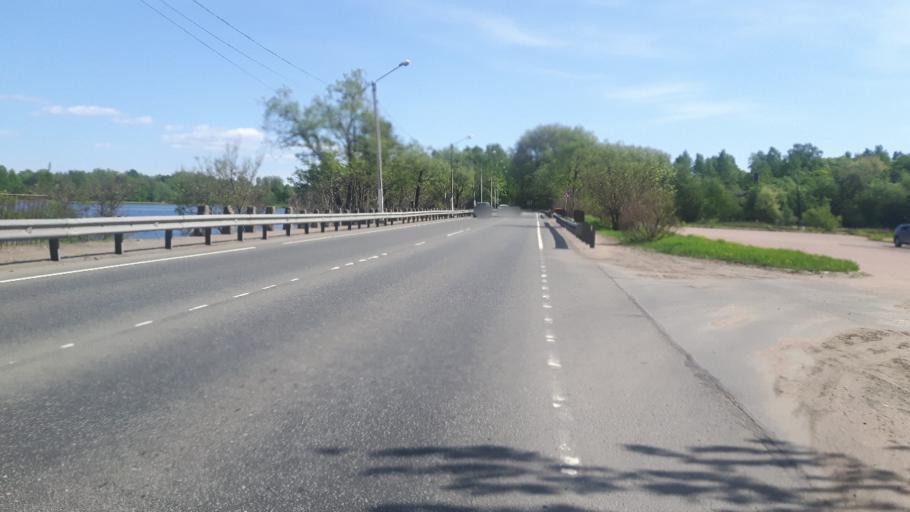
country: RU
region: Leningrad
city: Vyborg
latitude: 60.7263
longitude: 28.7067
